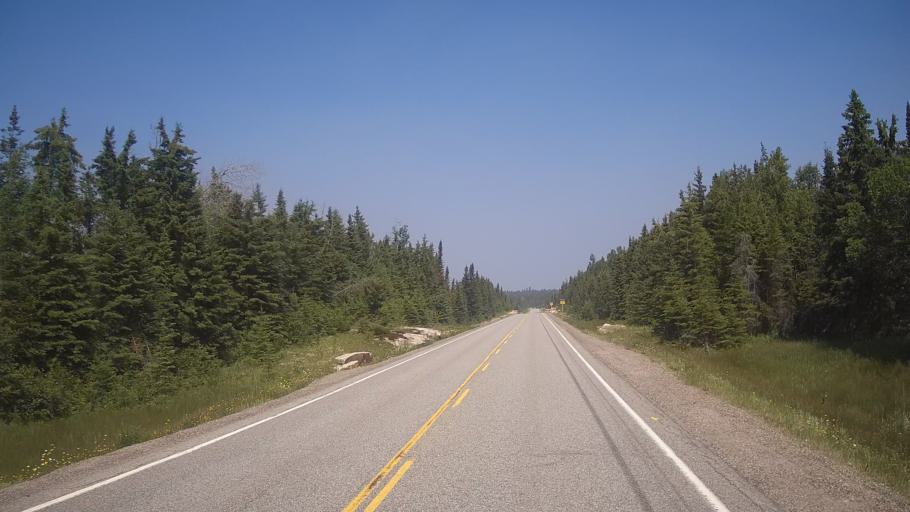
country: CA
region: Ontario
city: Timmins
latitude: 48.0666
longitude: -81.5881
